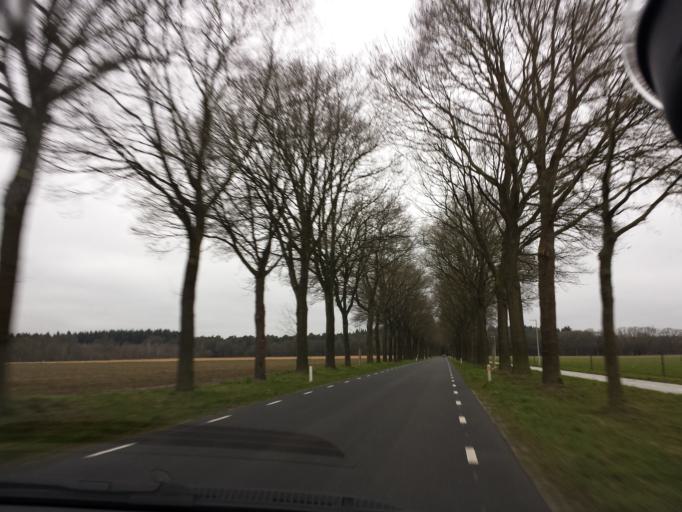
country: DE
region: North Rhine-Westphalia
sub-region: Regierungsbezirk Koln
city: Waldfeucht
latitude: 51.0898
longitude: 5.9603
